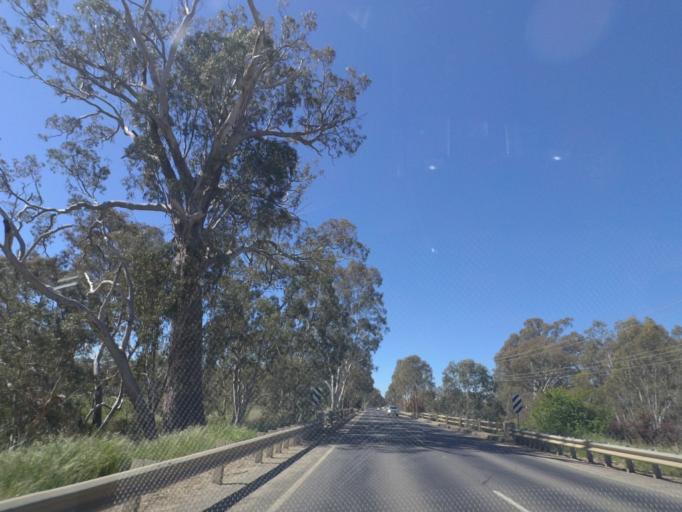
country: AU
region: Victoria
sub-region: Murrindindi
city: Kinglake West
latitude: -37.0254
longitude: 145.1113
